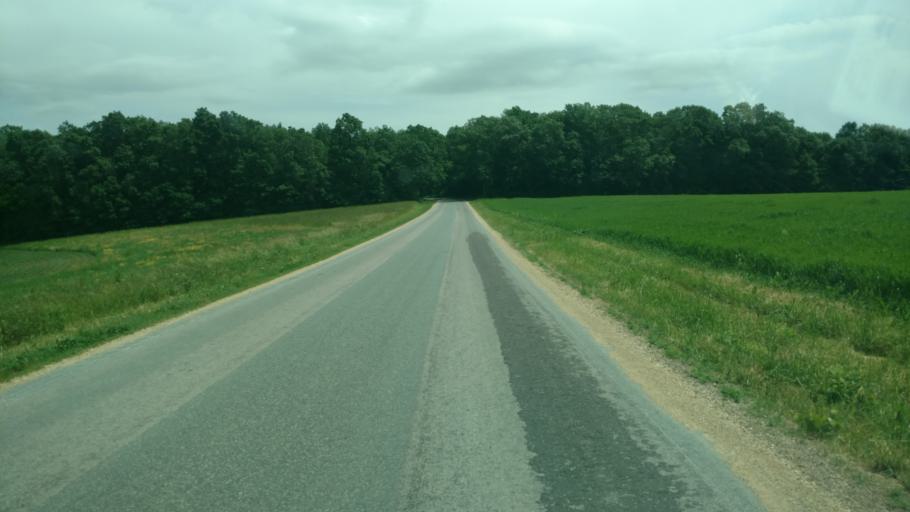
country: US
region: Wisconsin
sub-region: Monroe County
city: Cashton
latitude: 43.6921
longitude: -90.6635
